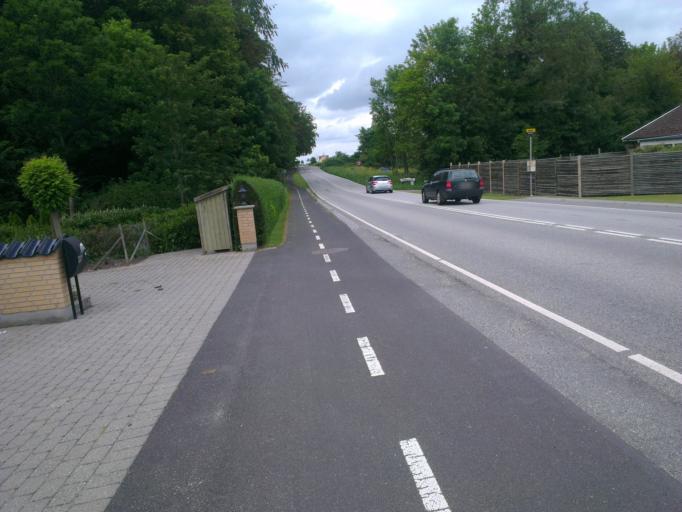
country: DK
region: Capital Region
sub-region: Frederikssund Kommune
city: Skibby
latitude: 55.6883
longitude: 11.9490
